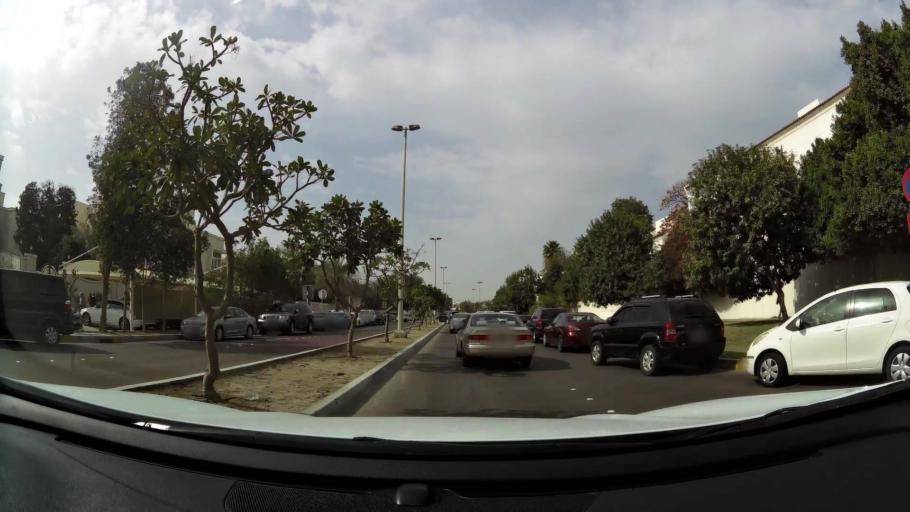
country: AE
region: Abu Dhabi
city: Abu Dhabi
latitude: 24.4467
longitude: 54.3863
